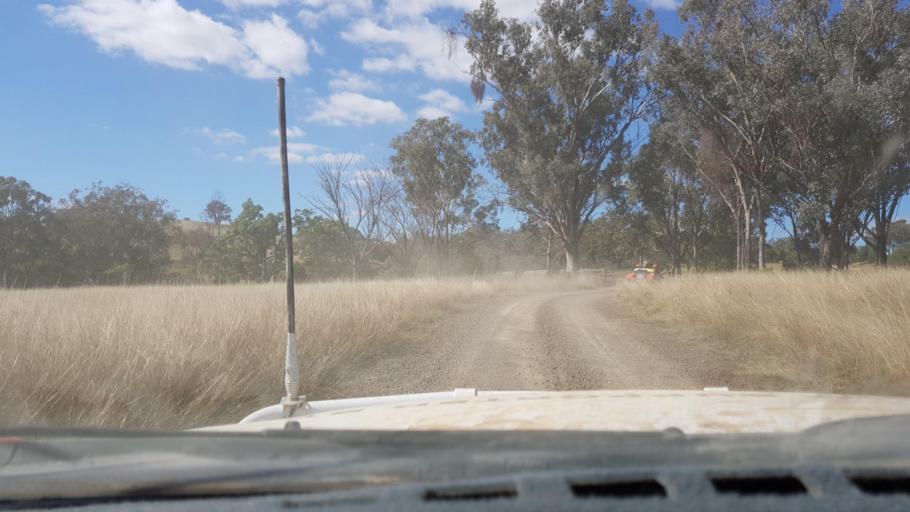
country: AU
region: New South Wales
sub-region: Tamworth Municipality
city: Manilla
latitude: -30.4288
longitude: 150.8184
